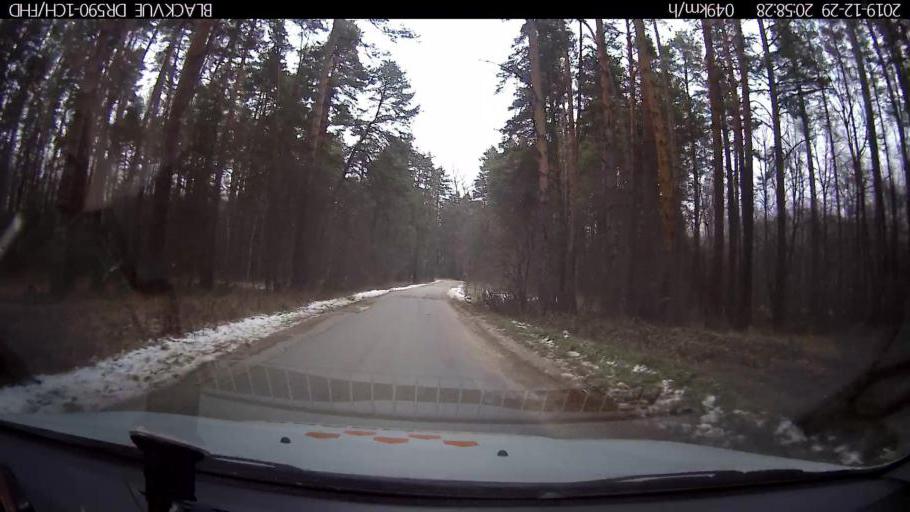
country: RU
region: Nizjnij Novgorod
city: Afonino
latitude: 56.1689
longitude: 43.9871
